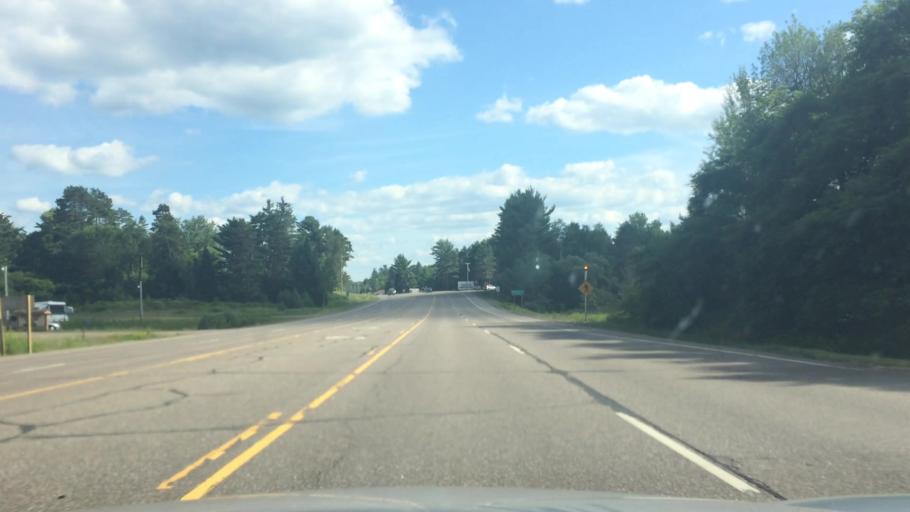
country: US
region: Wisconsin
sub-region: Vilas County
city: Lac du Flambeau
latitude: 45.8105
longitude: -89.7257
